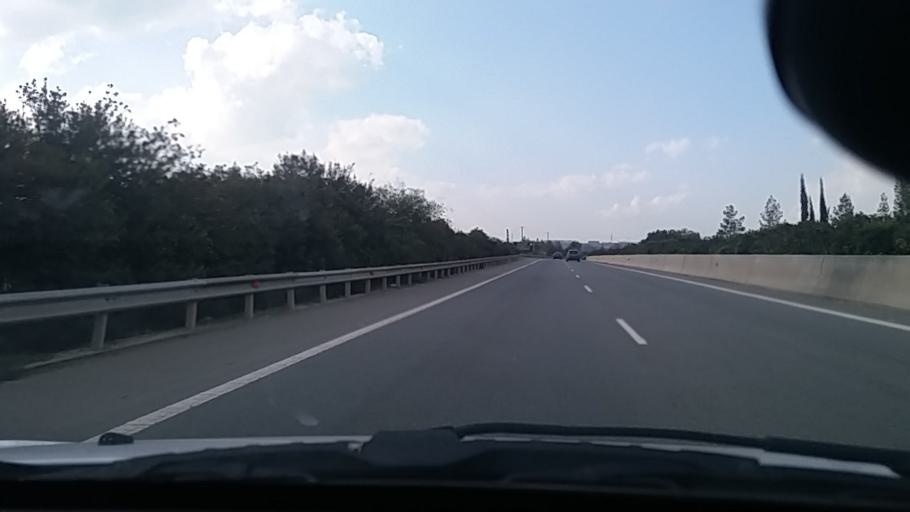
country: CY
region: Lefkosia
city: Kokkinotrimithia
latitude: 35.1453
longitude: 33.2551
